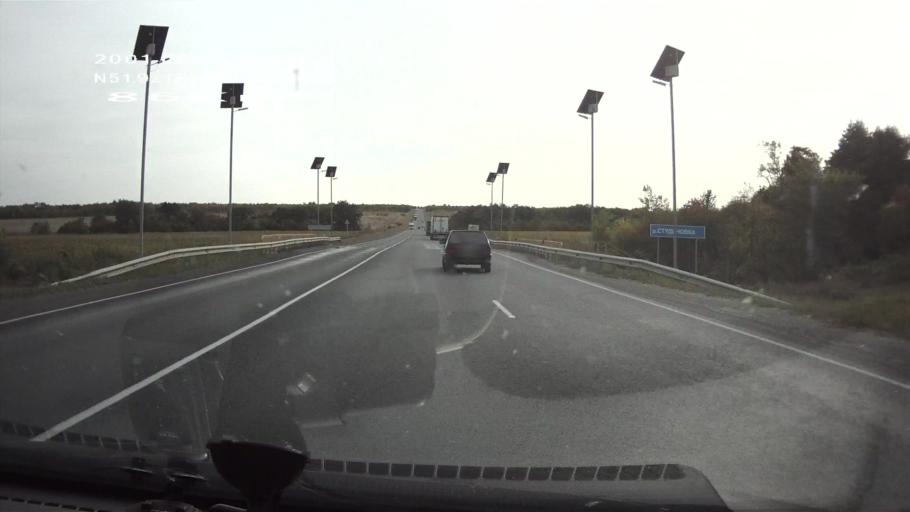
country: RU
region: Saratov
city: Sinodskoye
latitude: 51.9210
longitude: 46.5610
